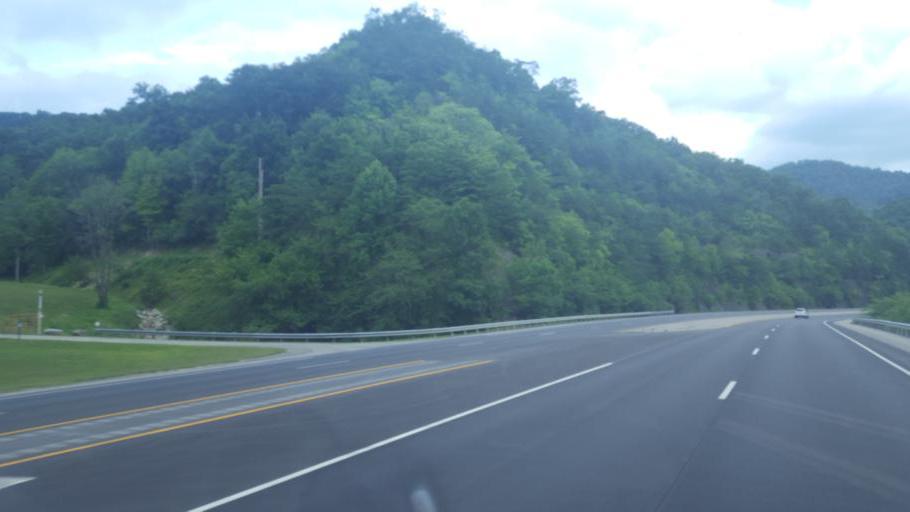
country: US
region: Kentucky
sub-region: Pike County
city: Pikeville
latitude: 37.3486
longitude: -82.5494
